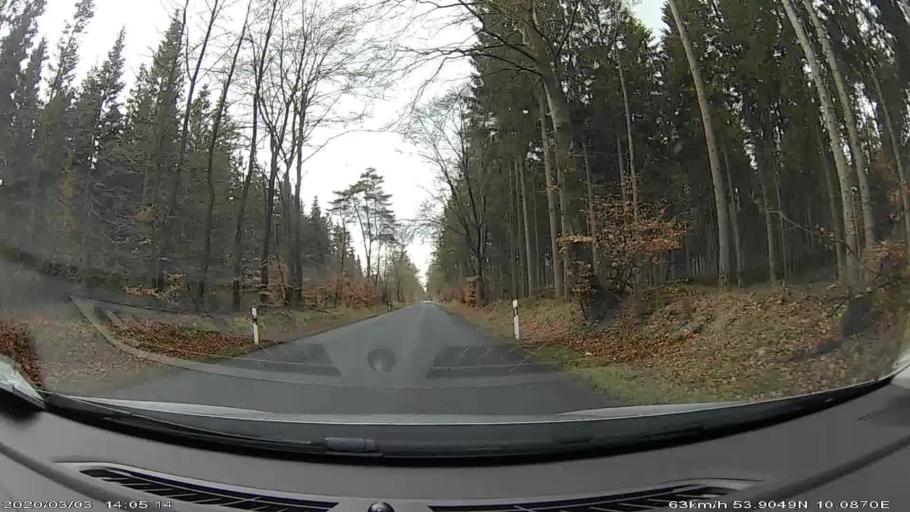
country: DE
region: Schleswig-Holstein
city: Hartenholm
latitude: 53.9045
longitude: 10.0861
